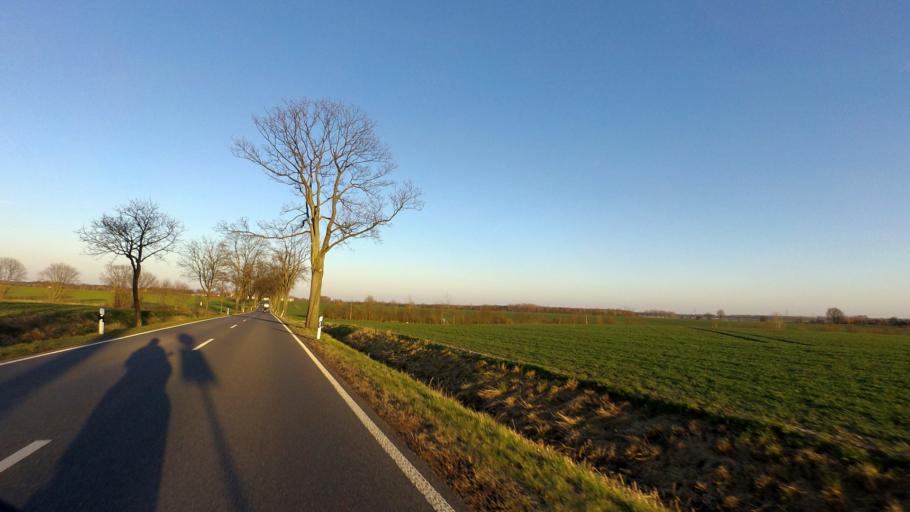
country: DE
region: Brandenburg
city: Ahrensfelde
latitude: 52.5721
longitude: 13.6021
